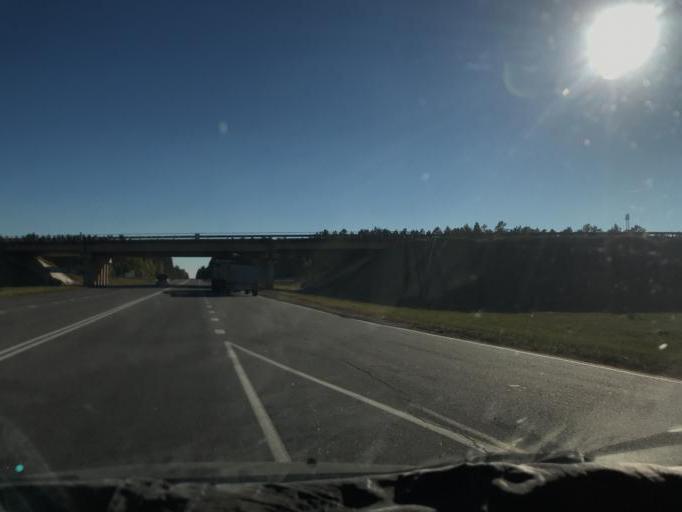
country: BY
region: Gomel
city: Kalinkavichy
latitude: 52.0743
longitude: 29.3610
